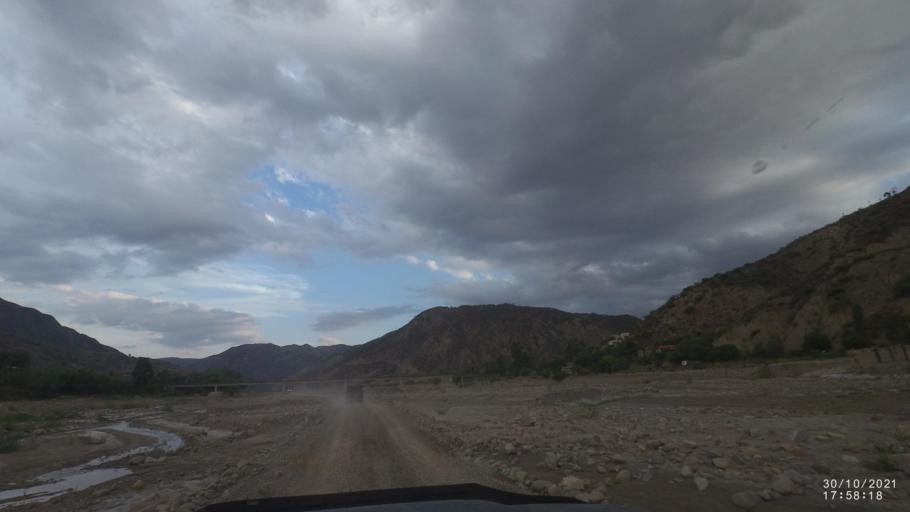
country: BO
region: Cochabamba
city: Sipe Sipe
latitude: -17.5530
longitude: -66.4769
